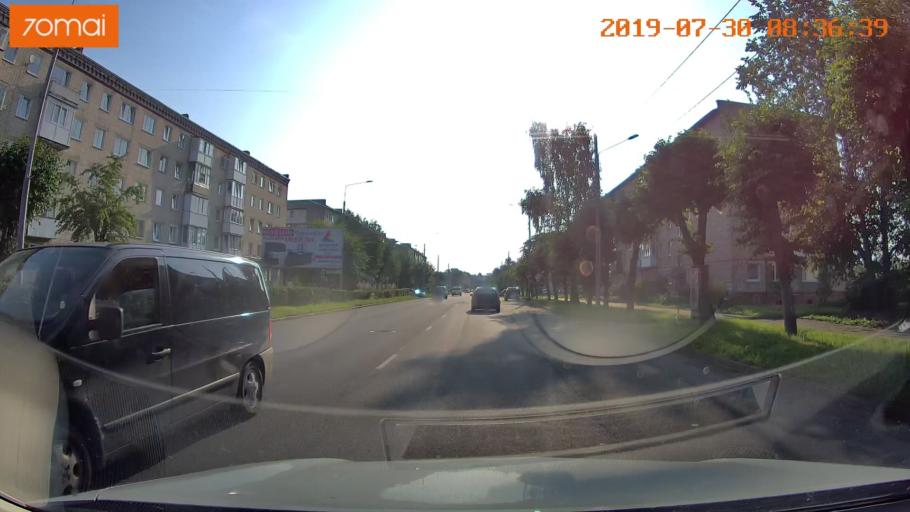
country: RU
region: Kaliningrad
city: Chernyakhovsk
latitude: 54.6354
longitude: 21.7963
